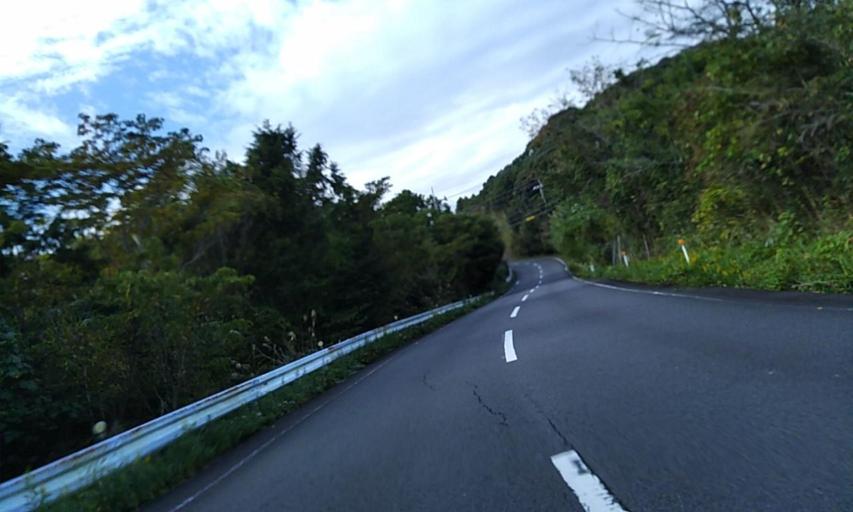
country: JP
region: Wakayama
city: Shingu
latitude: 33.4696
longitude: 135.8211
